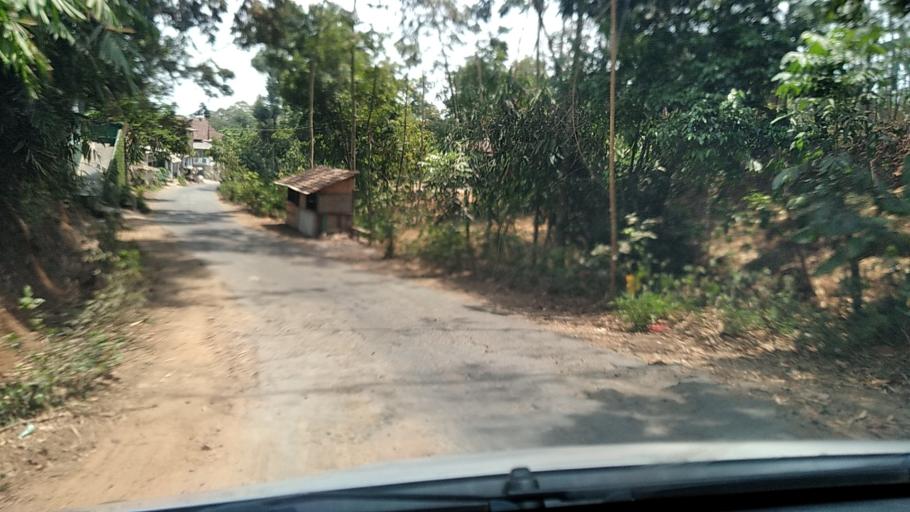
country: ID
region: Central Java
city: Ungaran
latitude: -7.1070
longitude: 110.3328
